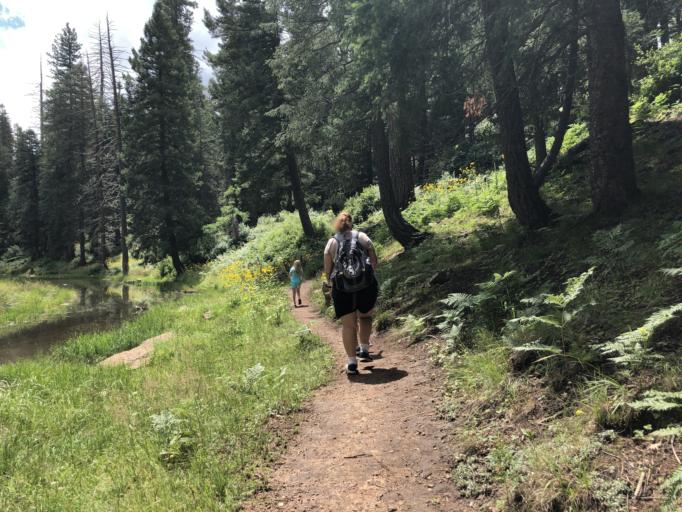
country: US
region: Arizona
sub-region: Gila County
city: Star Valley
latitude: 34.3397
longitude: -110.9554
